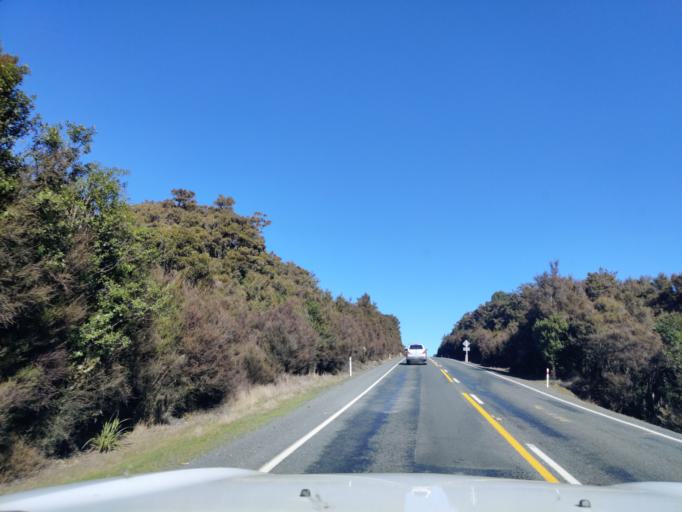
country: NZ
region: Waikato
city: Turangi
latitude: -39.1437
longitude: 175.7715
